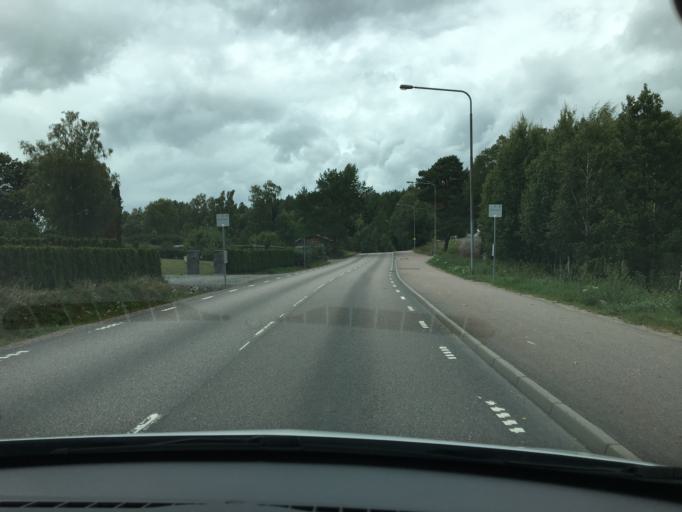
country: SE
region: Vaestra Goetaland
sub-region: Ale Kommun
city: Nodinge-Nol
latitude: 57.8888
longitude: 12.0748
